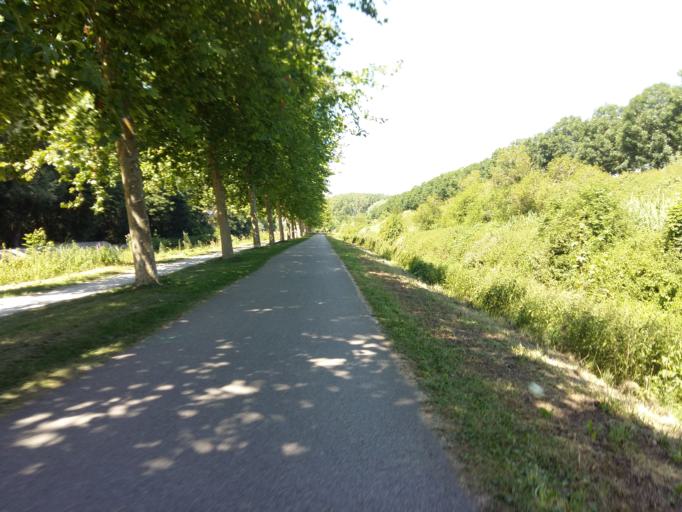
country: FR
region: Picardie
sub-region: Departement de la Somme
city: Dreuil-les-Amiens
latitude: 49.9170
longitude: 2.2634
